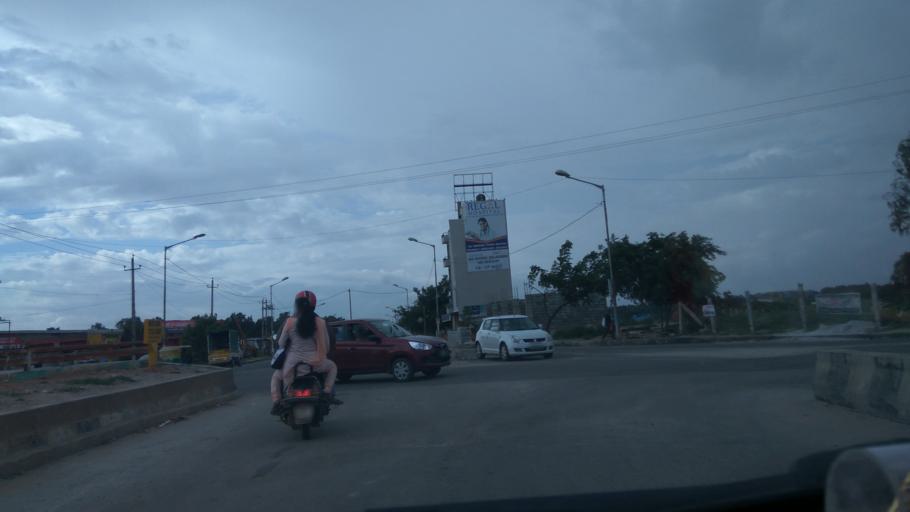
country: IN
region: Karnataka
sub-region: Bangalore Urban
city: Yelahanka
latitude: 13.1016
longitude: 77.6348
